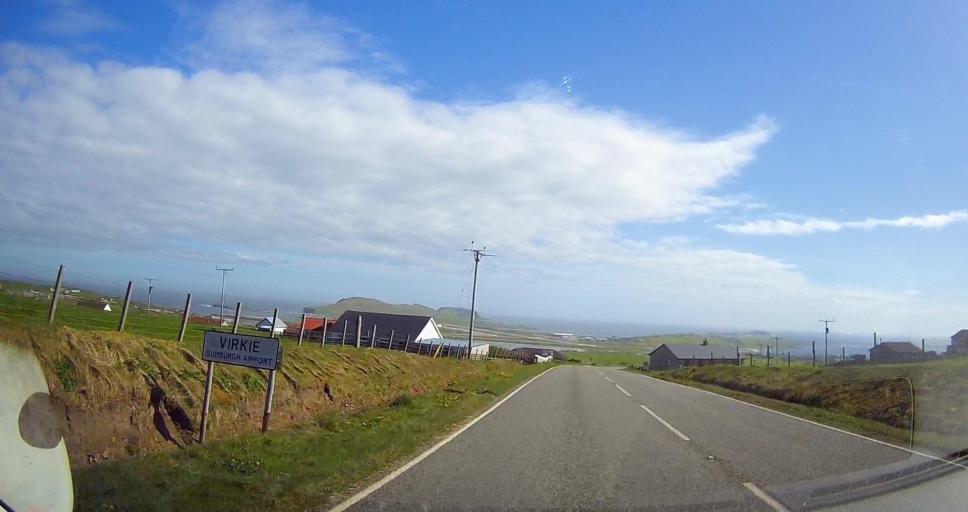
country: GB
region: Scotland
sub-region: Shetland Islands
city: Sandwick
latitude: 59.8964
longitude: -1.3034
